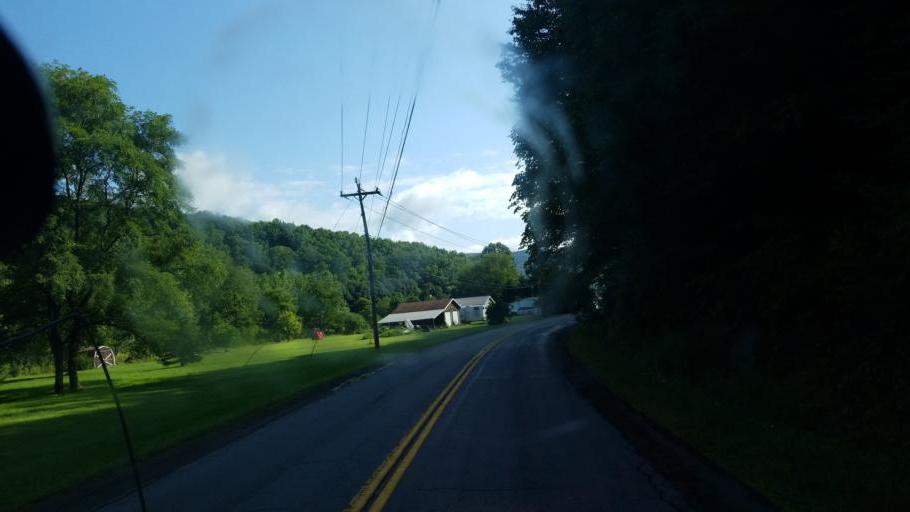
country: US
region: New York
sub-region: Steuben County
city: Canisteo
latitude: 42.2603
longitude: -77.6208
